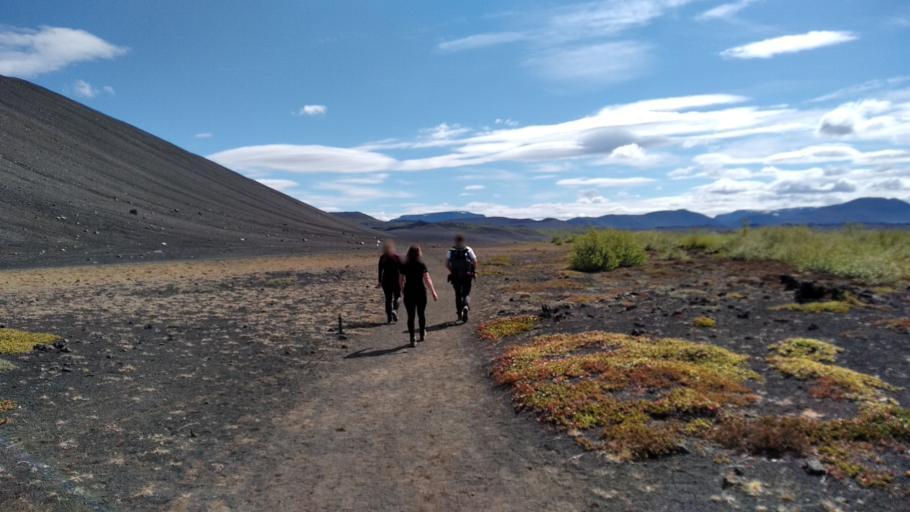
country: IS
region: Northeast
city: Laugar
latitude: 65.5991
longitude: -16.8875
